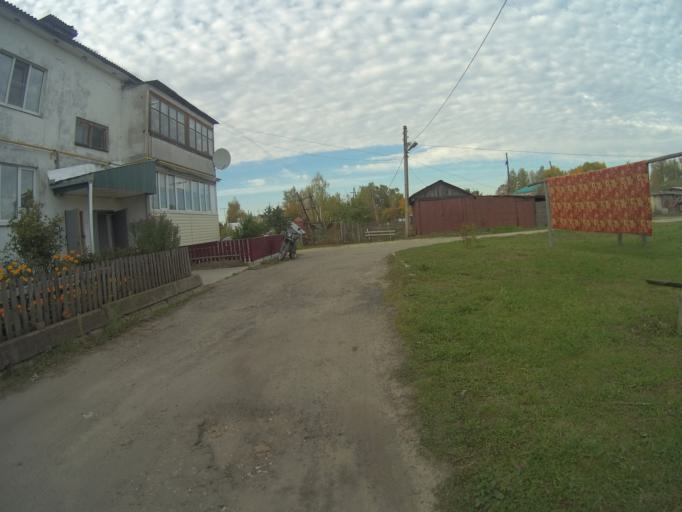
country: RU
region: Vladimir
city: Golovino
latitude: 55.9576
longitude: 40.4273
